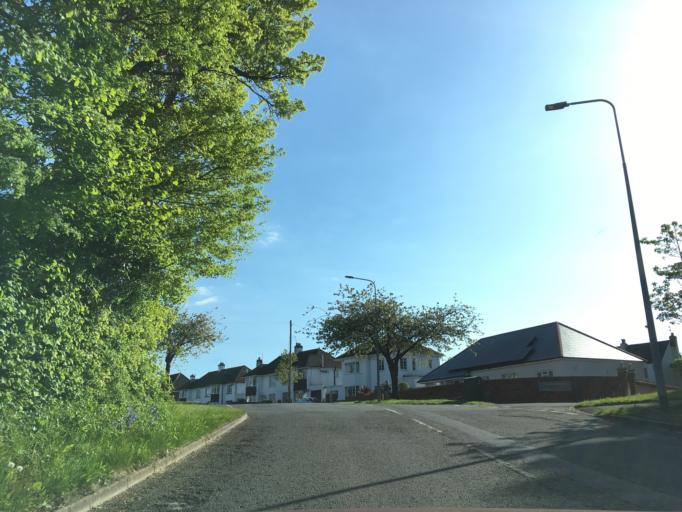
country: GB
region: Wales
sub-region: Cardiff
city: Cardiff
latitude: 51.5290
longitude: -3.1658
